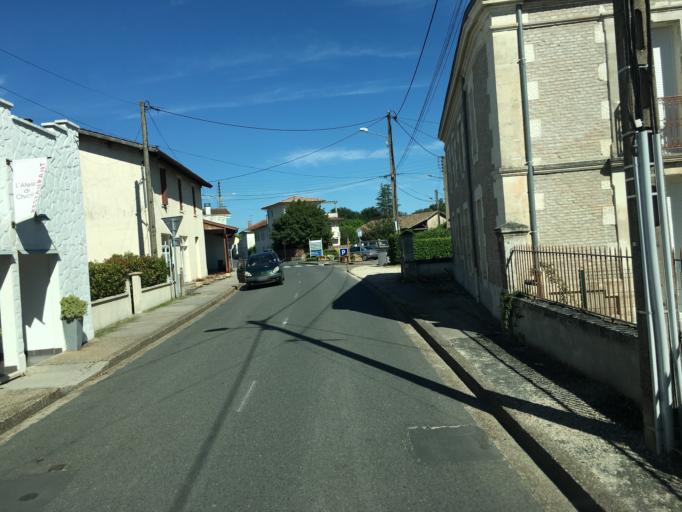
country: FR
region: Aquitaine
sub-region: Departement de la Gironde
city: Belin-Beliet
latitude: 44.5080
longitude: -0.7871
